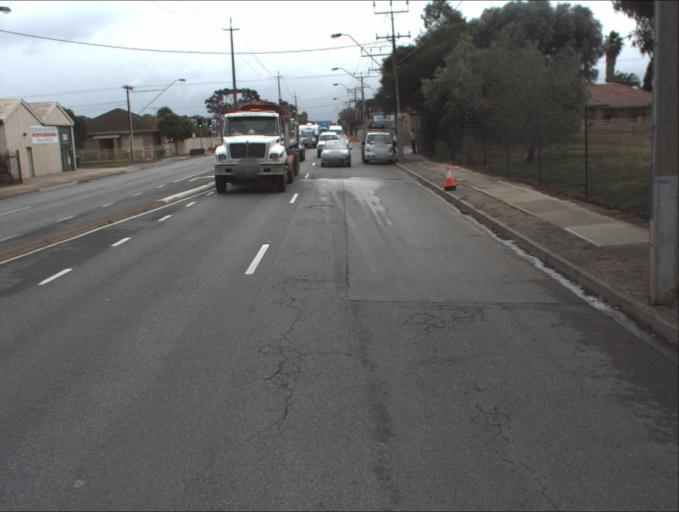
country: AU
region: South Australia
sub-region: Prospect
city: Prospect
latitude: -34.8796
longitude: 138.5716
